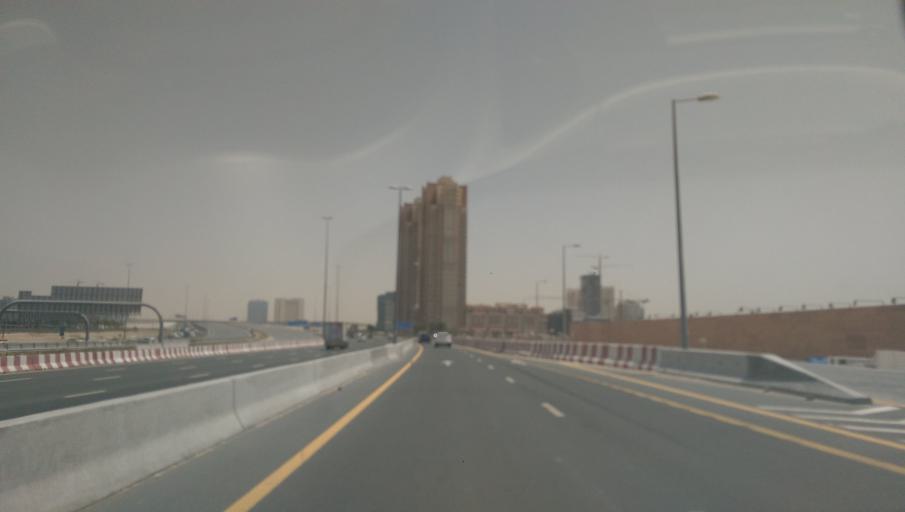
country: AE
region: Dubai
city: Dubai
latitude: 25.0528
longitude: 55.1948
